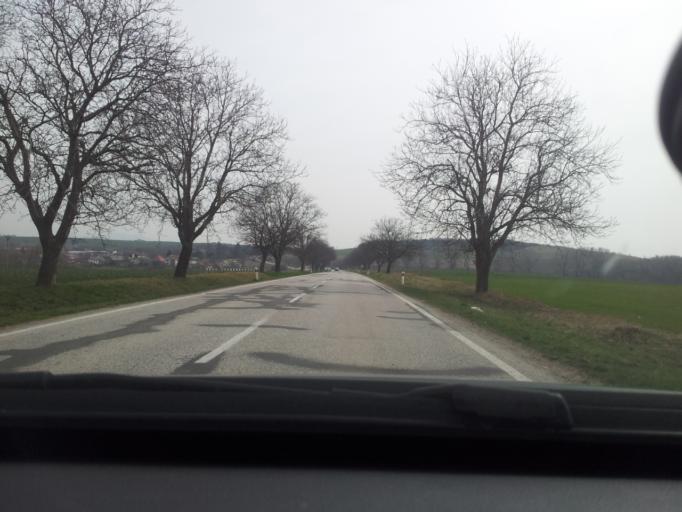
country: SK
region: Trnavsky
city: Hlohovec
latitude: 48.3595
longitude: 17.9262
